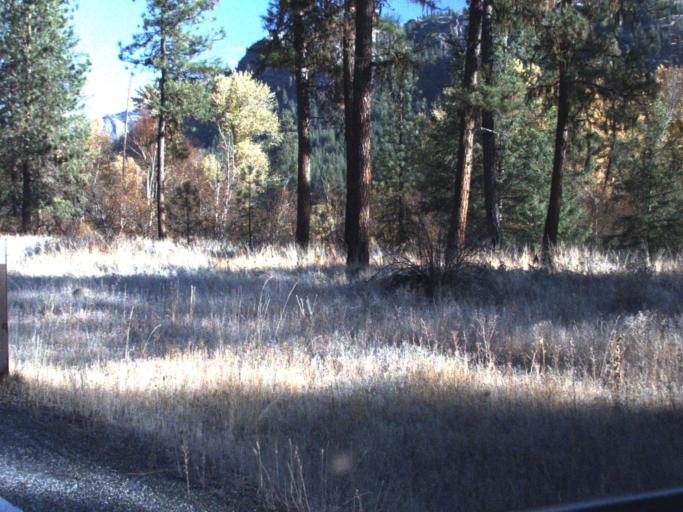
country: US
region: Washington
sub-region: Ferry County
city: Republic
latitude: 48.3259
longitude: -118.7445
